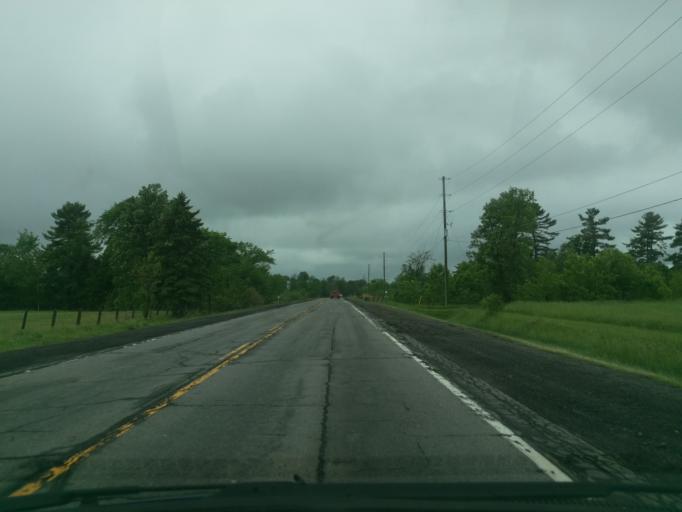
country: CA
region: Ontario
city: Clarence-Rockland
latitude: 45.5198
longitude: -75.3633
